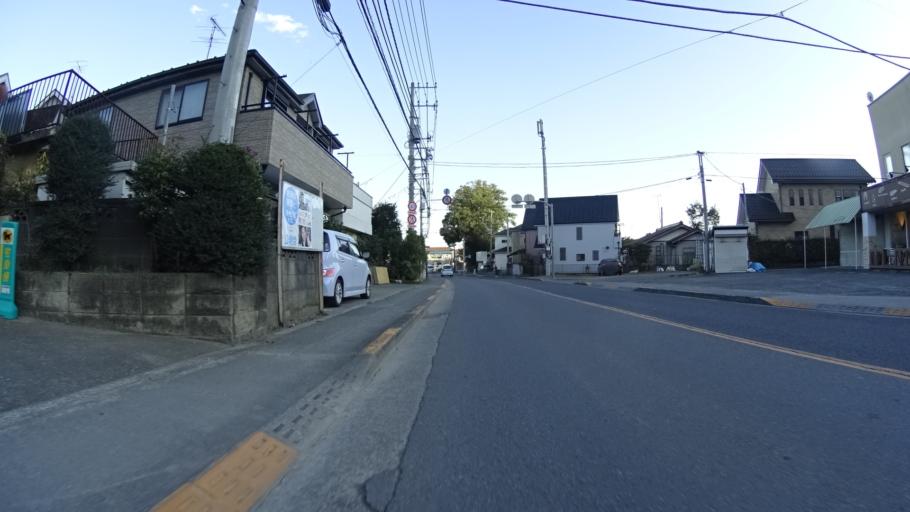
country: JP
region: Tokyo
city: Hachioji
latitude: 35.6812
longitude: 139.2775
